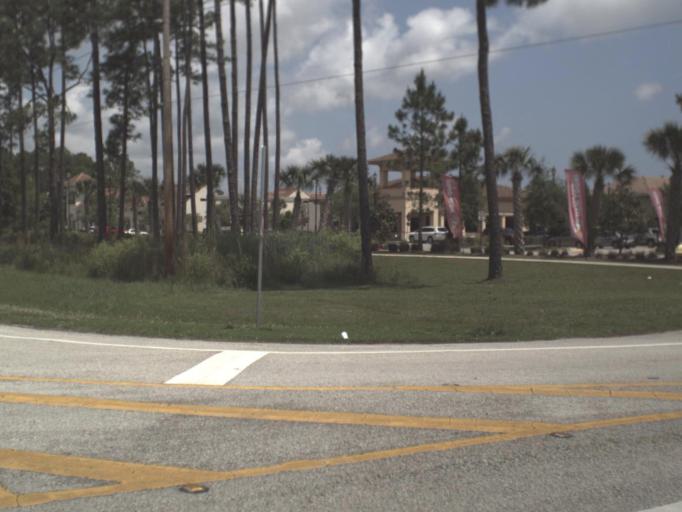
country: US
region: Florida
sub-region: Saint Johns County
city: Villano Beach
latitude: 30.0100
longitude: -81.3897
